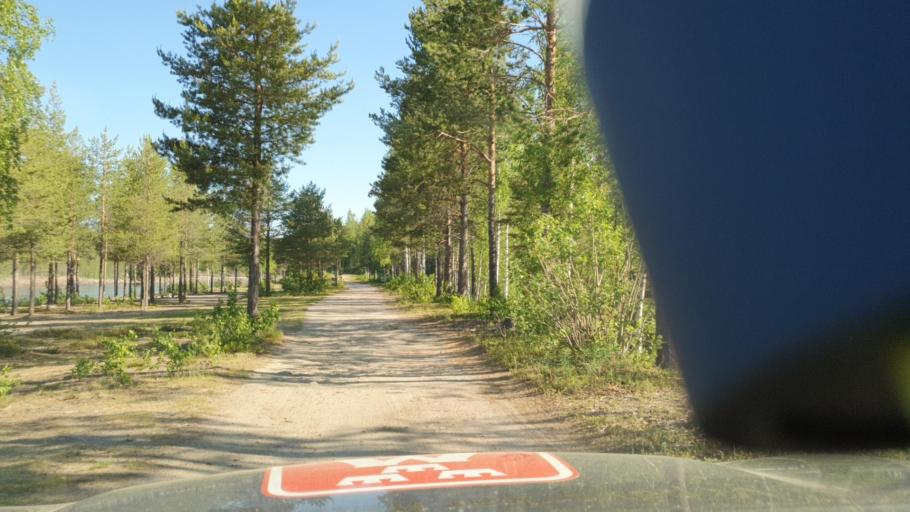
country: SE
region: Norrbotten
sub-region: Alvsbyns Kommun
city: AElvsbyn
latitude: 66.2185
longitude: 20.8604
